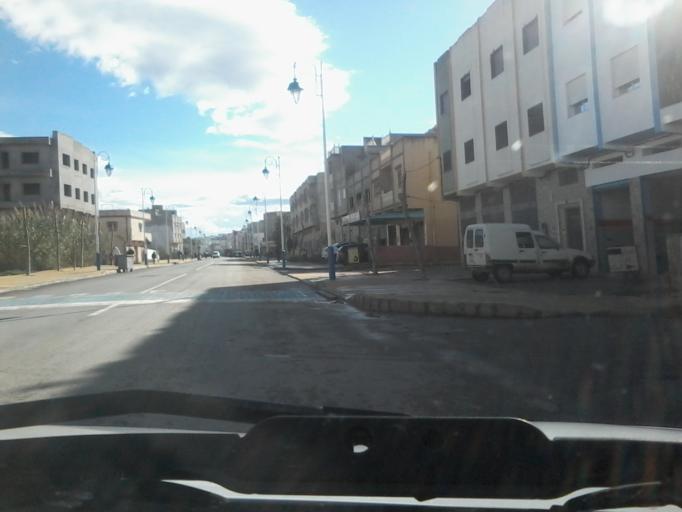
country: MA
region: Tanger-Tetouan
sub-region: Tetouan
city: Martil
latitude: 35.7009
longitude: -5.3499
